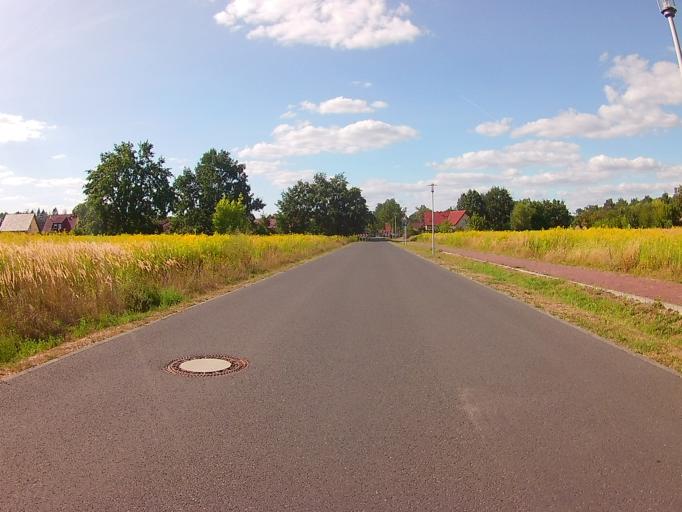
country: DE
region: Brandenburg
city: Zeuthen
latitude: 52.3621
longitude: 13.6154
